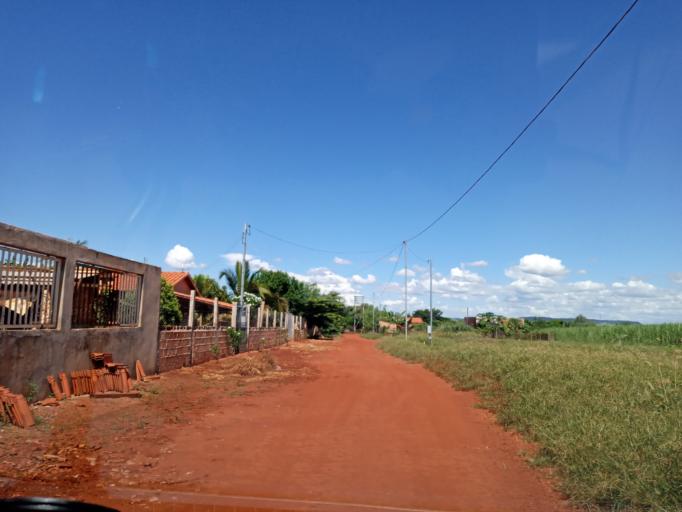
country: BR
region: Goias
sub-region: Itumbiara
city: Itumbiara
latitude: -18.4301
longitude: -49.1177
